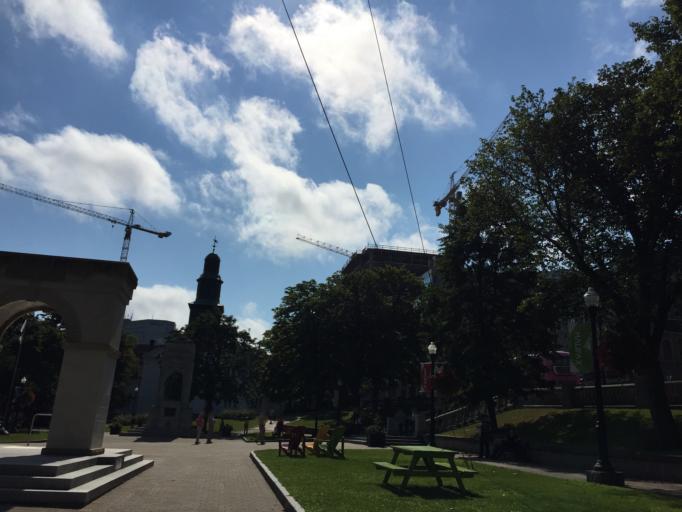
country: CA
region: Nova Scotia
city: Halifax
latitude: 44.6485
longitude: -63.5751
